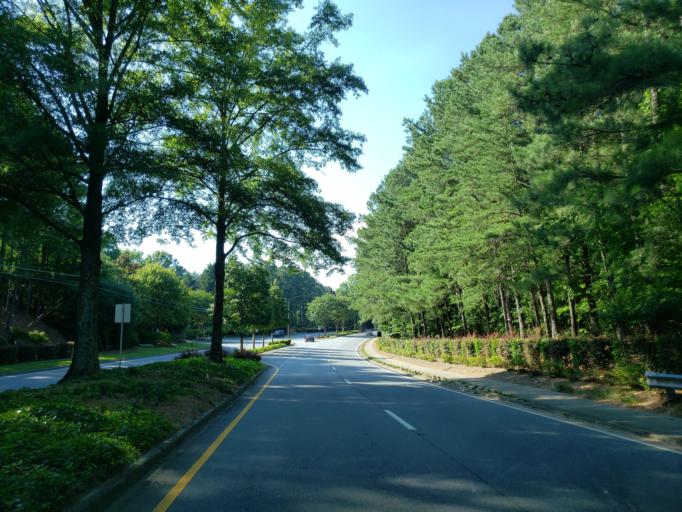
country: US
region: Georgia
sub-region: Cherokee County
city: Woodstock
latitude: 34.1264
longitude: -84.5595
